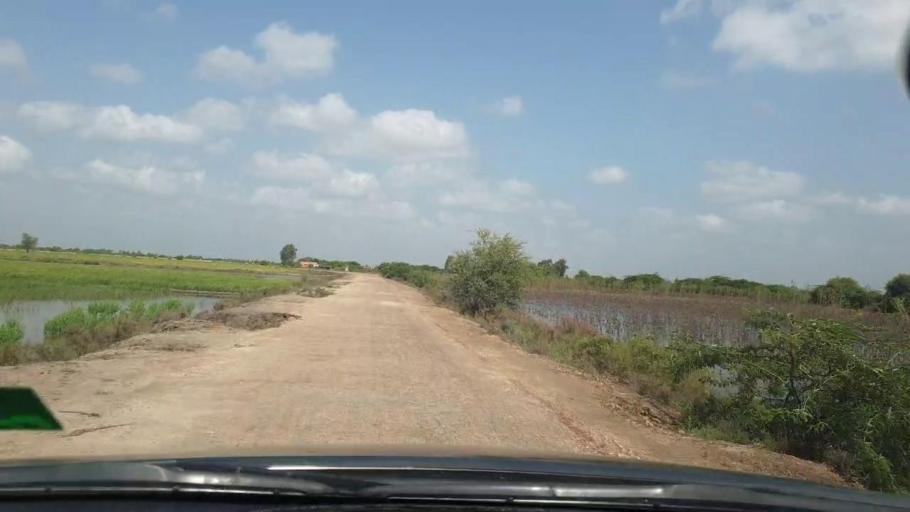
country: PK
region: Sindh
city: Tando Bago
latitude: 24.8634
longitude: 69.0575
